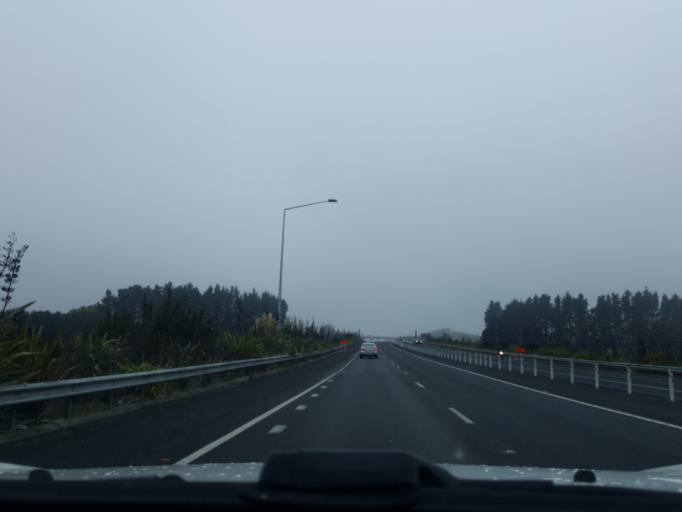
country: NZ
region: Waikato
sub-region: Waikato District
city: Ngaruawahia
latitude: -37.7029
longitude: 175.2093
